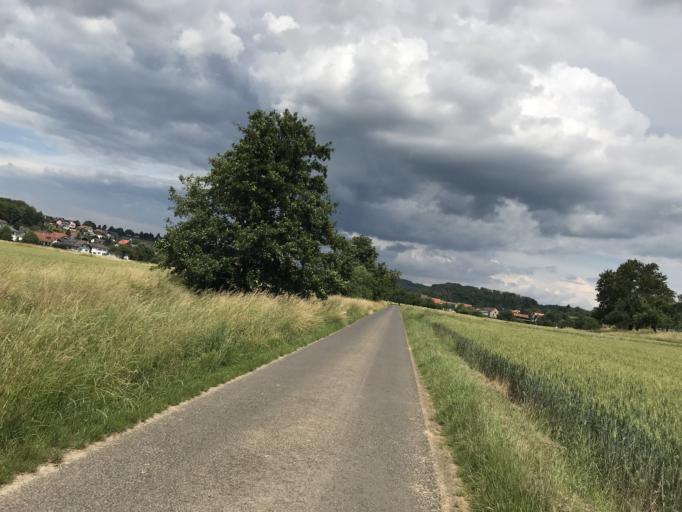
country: DE
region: Hesse
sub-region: Regierungsbezirk Giessen
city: Hungen
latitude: 50.4667
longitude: 8.9446
